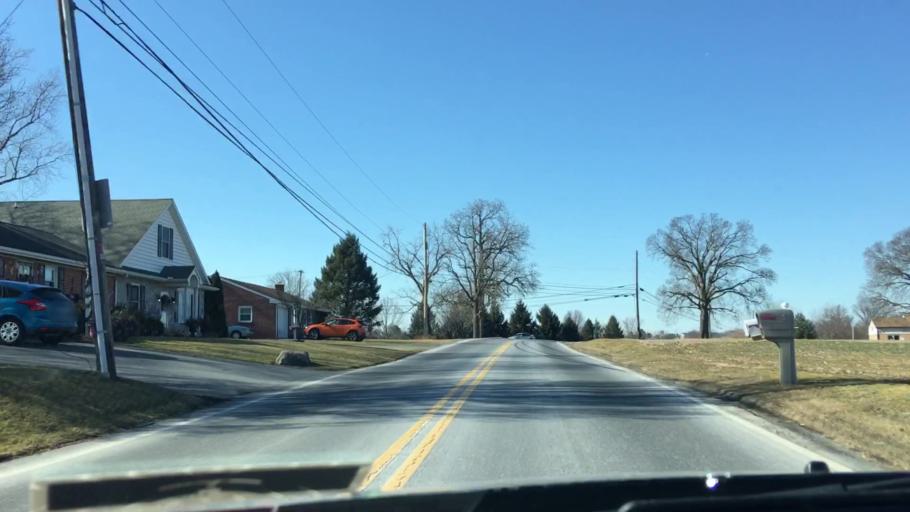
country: US
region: Pennsylvania
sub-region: Lancaster County
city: Lancaster
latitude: 40.0619
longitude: -76.2428
